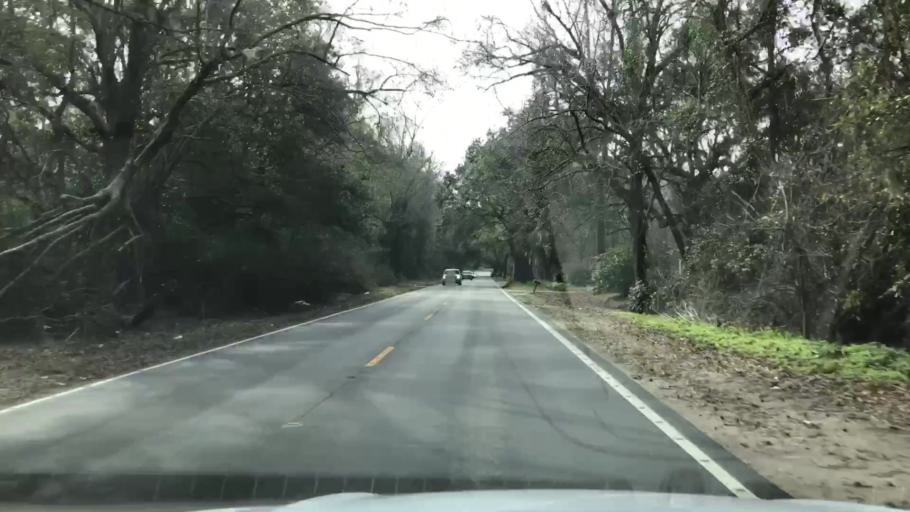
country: US
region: South Carolina
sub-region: Charleston County
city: Folly Beach
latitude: 32.6951
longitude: -80.0156
